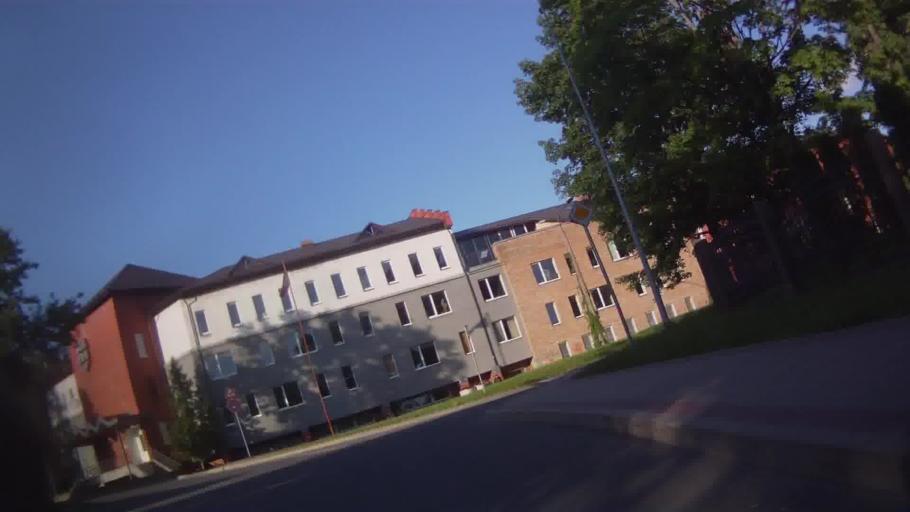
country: LV
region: Rezekne
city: Rezekne
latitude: 56.5043
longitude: 27.3360
